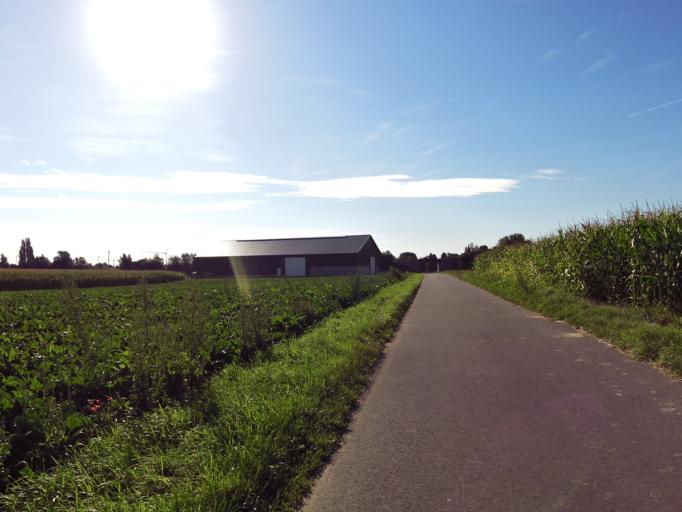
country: DE
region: North Rhine-Westphalia
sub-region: Regierungsbezirk Koln
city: Alsdorf
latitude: 50.8736
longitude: 6.1963
